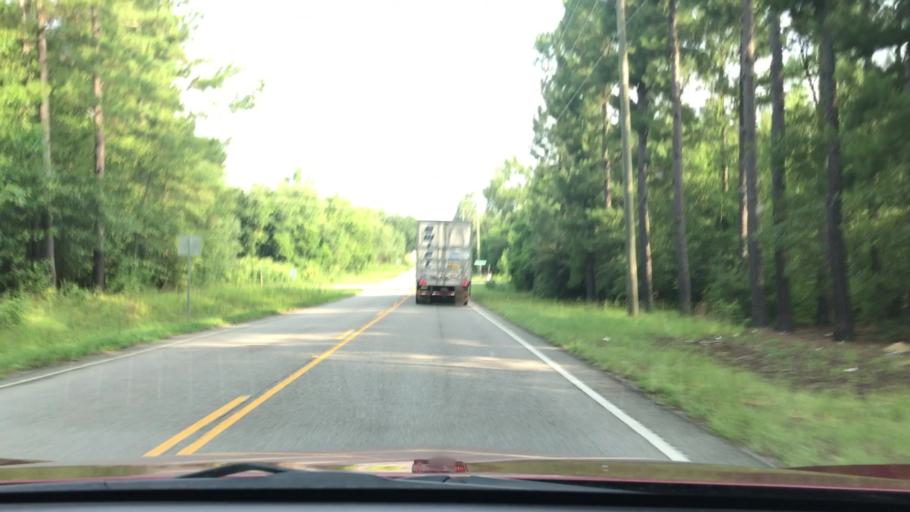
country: US
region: South Carolina
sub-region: Barnwell County
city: Blackville
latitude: 33.6028
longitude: -81.2645
